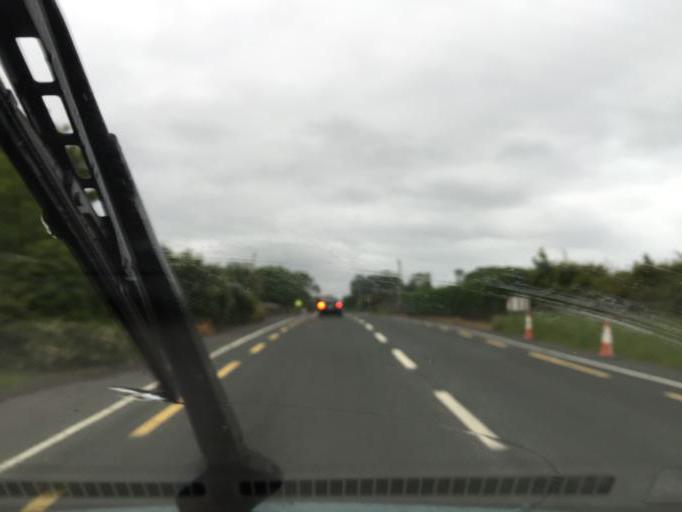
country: IE
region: Connaught
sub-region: Sligo
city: Strandhill
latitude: 54.2727
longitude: -8.5427
